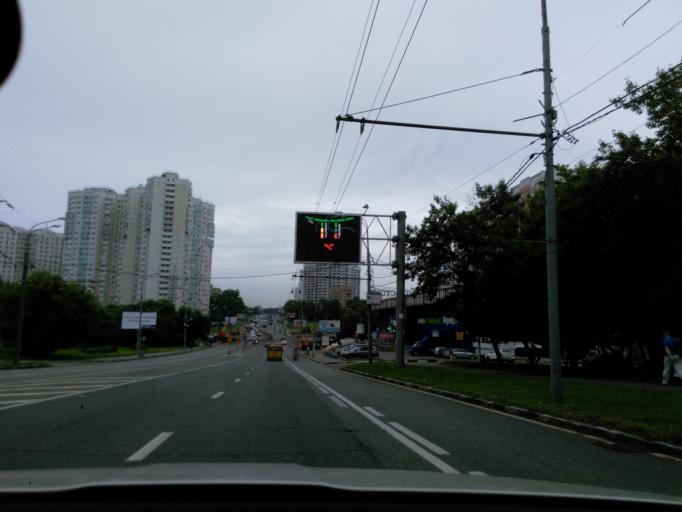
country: RU
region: Moscow
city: Tsaritsyno
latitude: 55.6403
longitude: 37.6553
